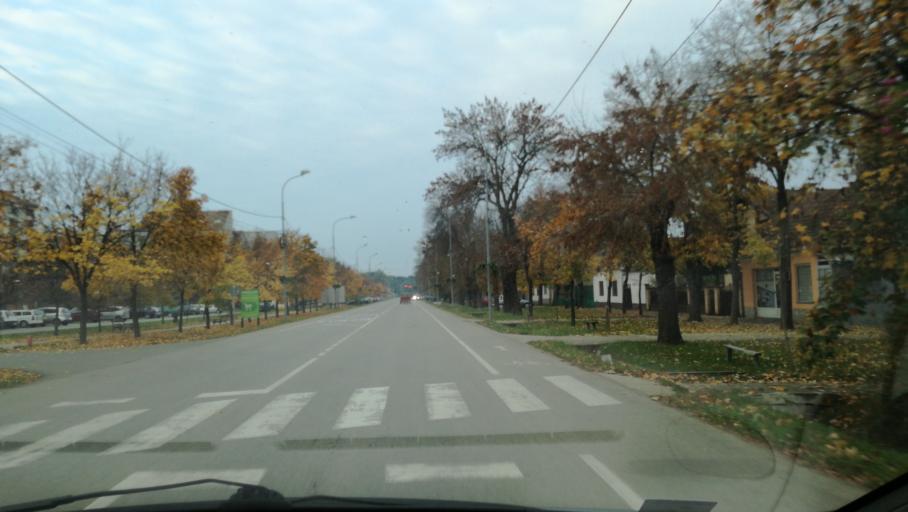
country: RS
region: Autonomna Pokrajina Vojvodina
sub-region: Severnobanatski Okrug
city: Kikinda
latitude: 45.8217
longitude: 20.4519
